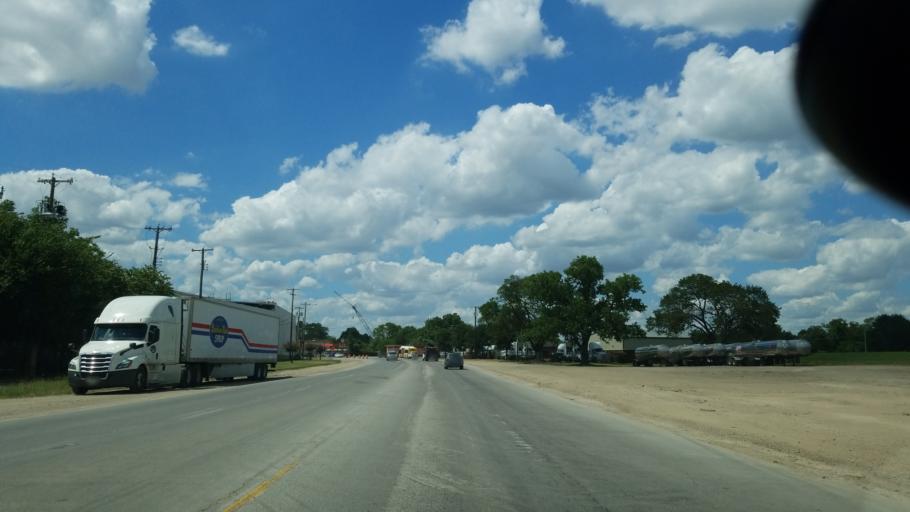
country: US
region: Texas
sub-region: Dallas County
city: Dallas
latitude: 32.7407
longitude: -96.7582
